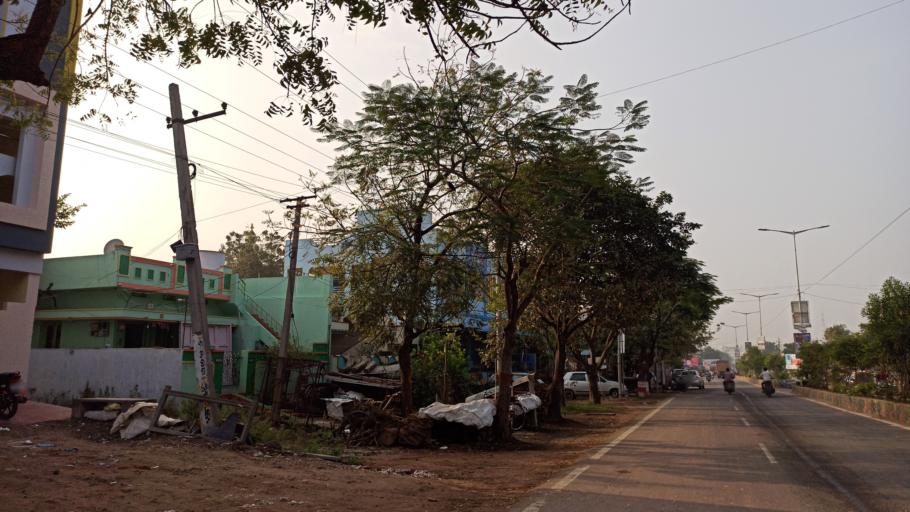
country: IN
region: Andhra Pradesh
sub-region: Guntur
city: Narasaraopet
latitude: 16.2490
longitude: 80.0570
